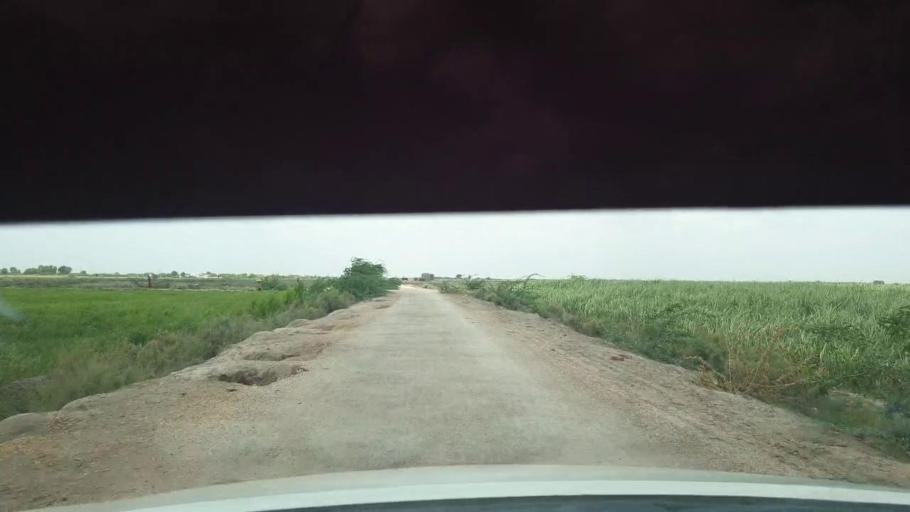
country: PK
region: Sindh
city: Kadhan
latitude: 24.5453
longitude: 69.1252
